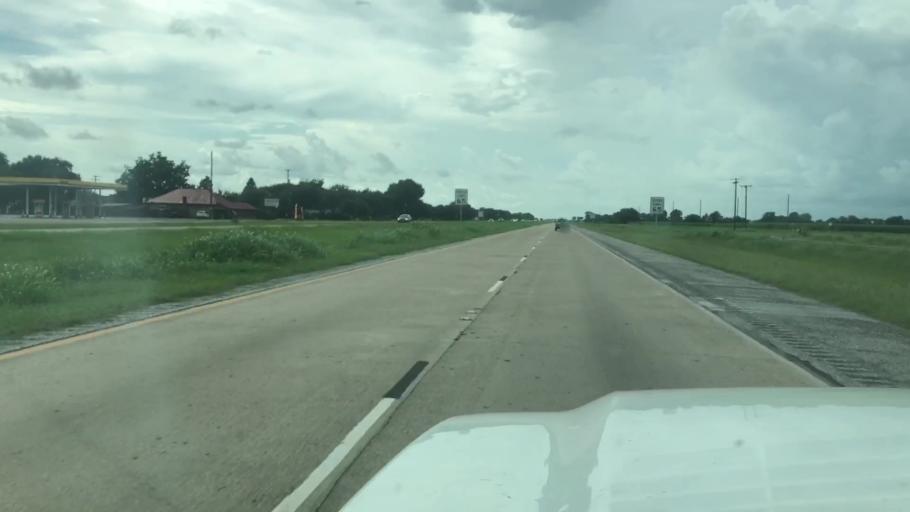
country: US
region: Louisiana
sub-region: Iberia Parish
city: Jeanerette
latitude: 29.8725
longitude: -91.6453
